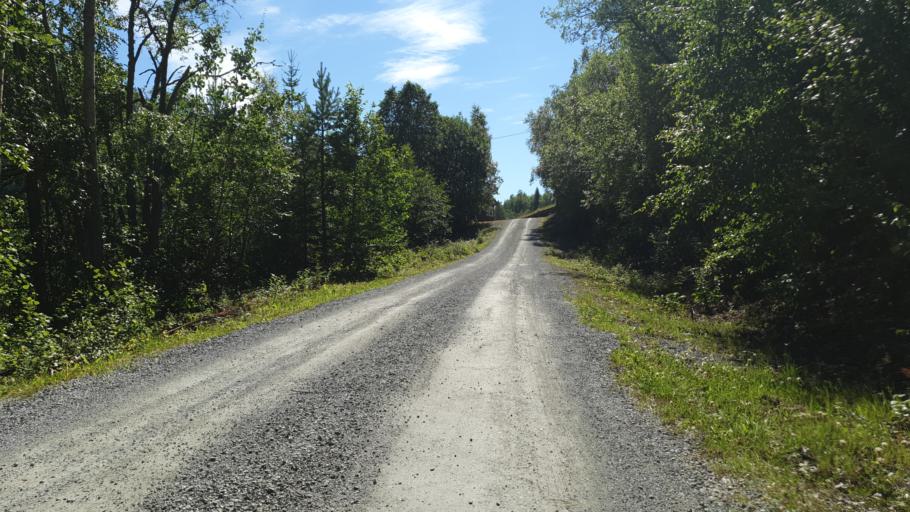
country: NO
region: Sor-Trondelag
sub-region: Meldal
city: Meldal
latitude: 63.1229
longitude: 9.7017
